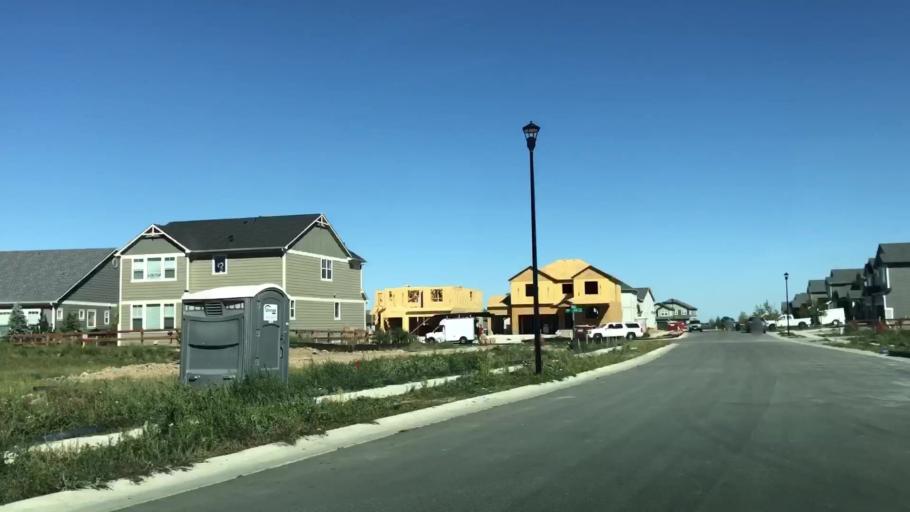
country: US
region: Colorado
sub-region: Larimer County
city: Fort Collins
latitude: 40.5035
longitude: -105.0332
